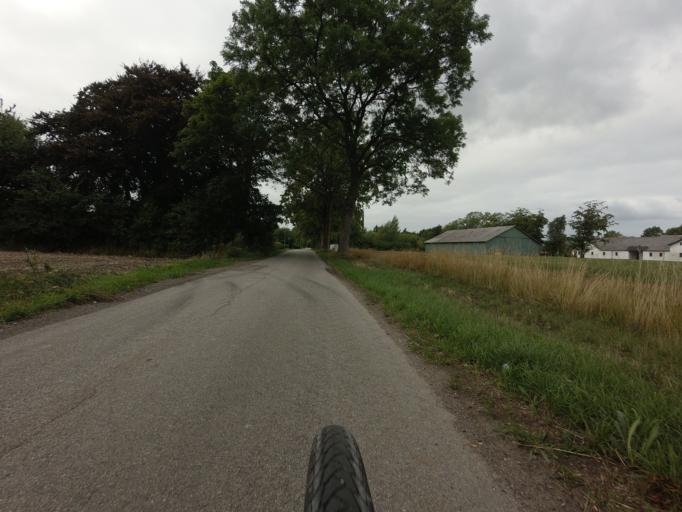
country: DK
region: Zealand
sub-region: Stevns Kommune
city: Store Heddinge
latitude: 55.3405
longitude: 12.4169
